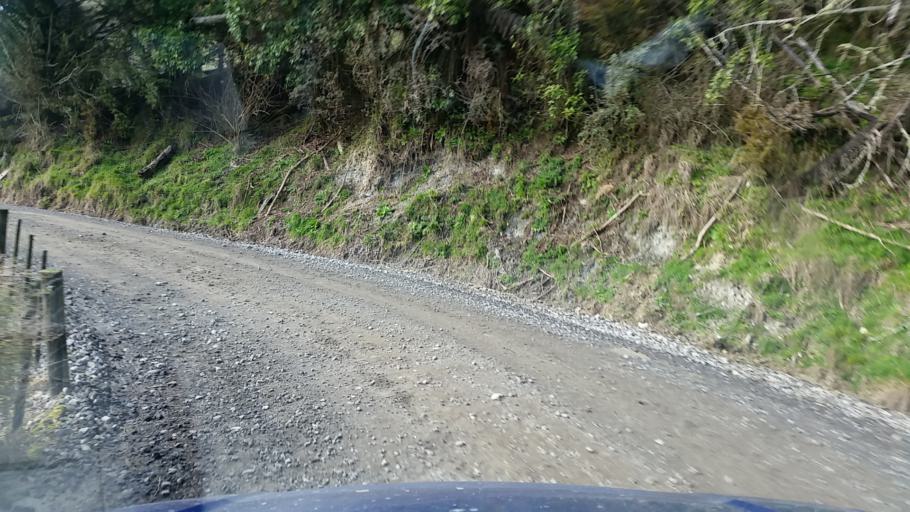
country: NZ
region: Taranaki
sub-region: New Plymouth District
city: Waitara
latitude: -39.0746
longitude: 174.8038
